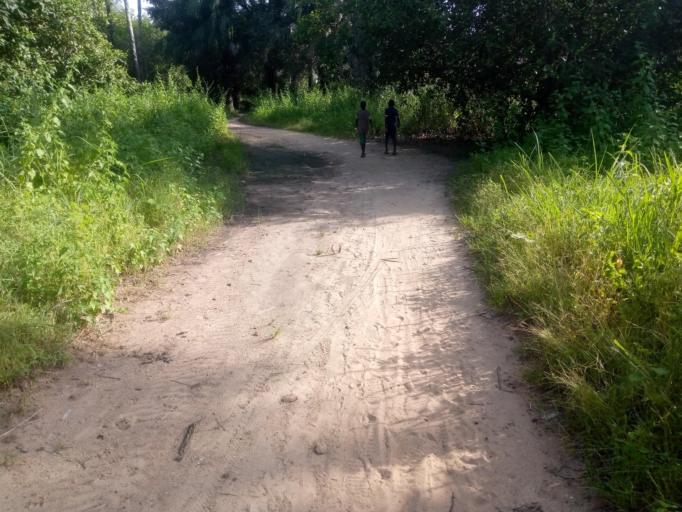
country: GM
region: Western
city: Gunjur
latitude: 13.0418
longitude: -16.7294
